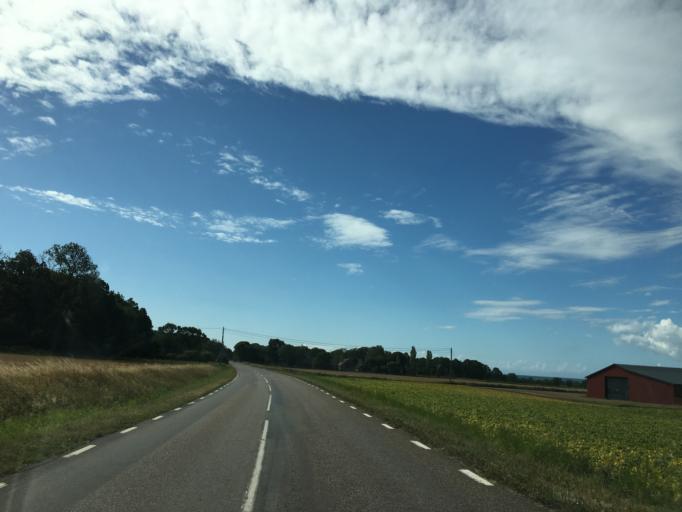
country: SE
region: Kalmar
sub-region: Morbylanga Kommun
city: Moerbylanga
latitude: 56.4357
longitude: 16.4197
